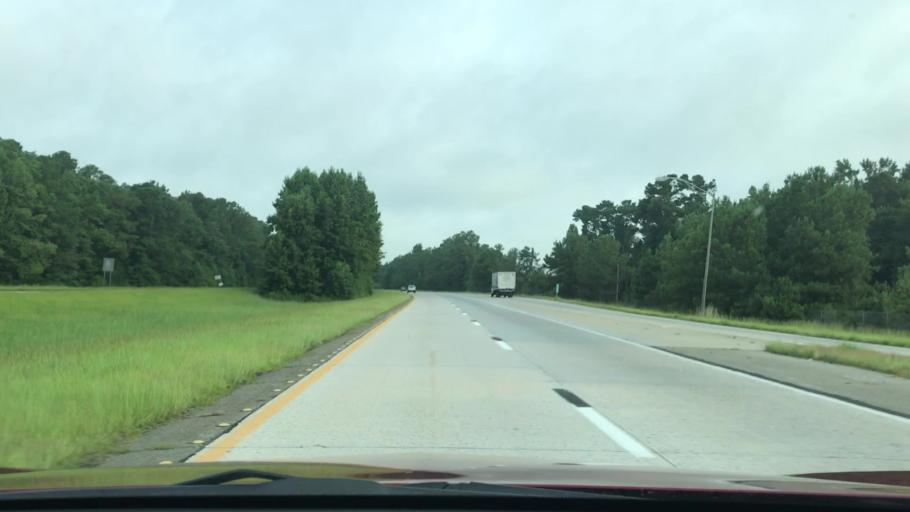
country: US
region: South Carolina
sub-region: Orangeburg County
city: Holly Hill
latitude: 33.2623
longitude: -80.4783
